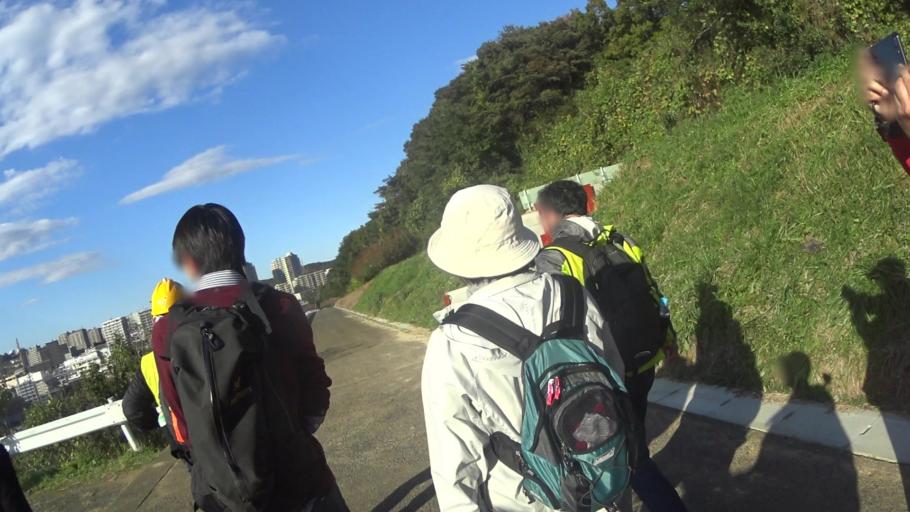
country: JP
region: Tokyo
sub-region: Machida-shi
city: Machida
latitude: 35.6148
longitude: 139.4765
